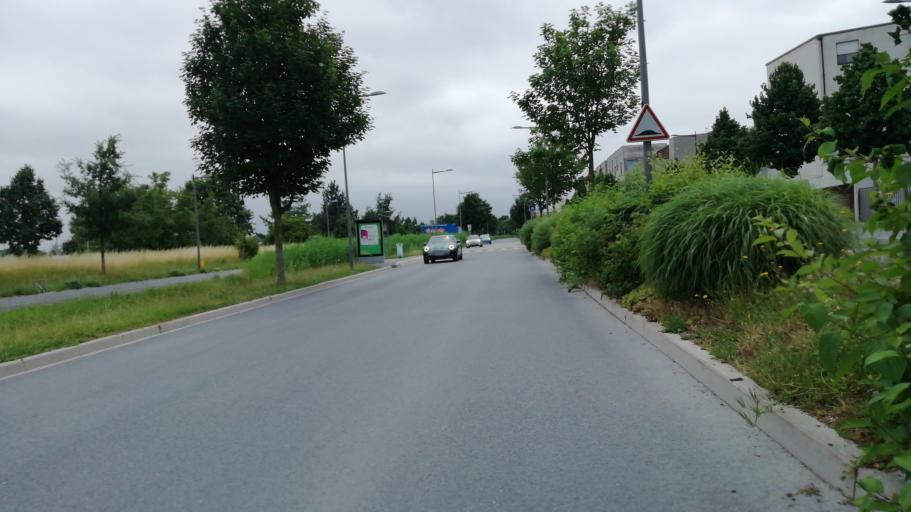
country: FR
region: Champagne-Ardenne
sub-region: Departement de la Marne
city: Betheny
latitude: 49.2607
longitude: 4.0623
